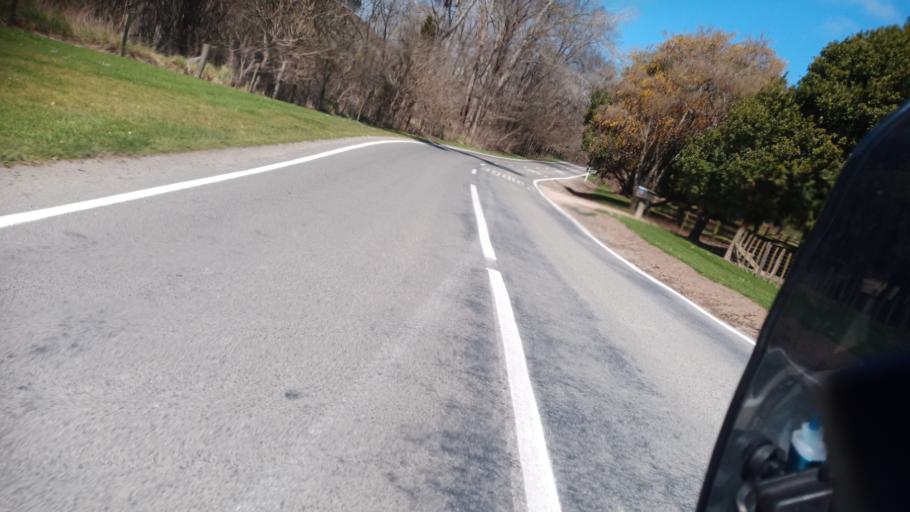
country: NZ
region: Gisborne
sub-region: Gisborne District
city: Gisborne
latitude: -38.7310
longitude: 177.8259
